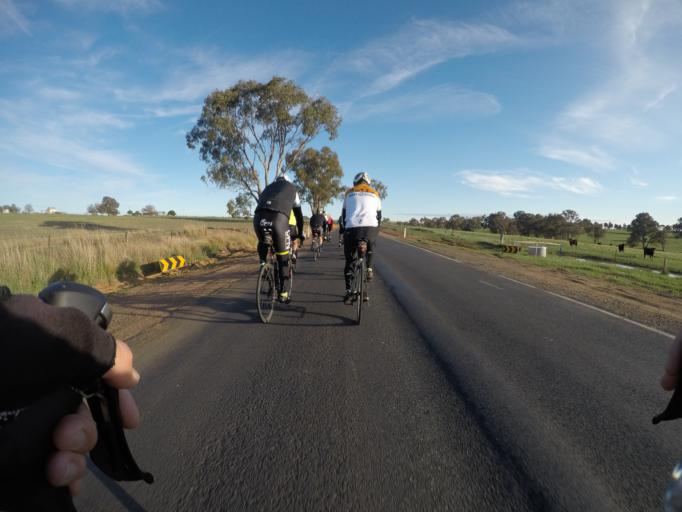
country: AU
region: New South Wales
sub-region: Cabonne
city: Molong
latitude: -33.0223
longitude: 148.8019
